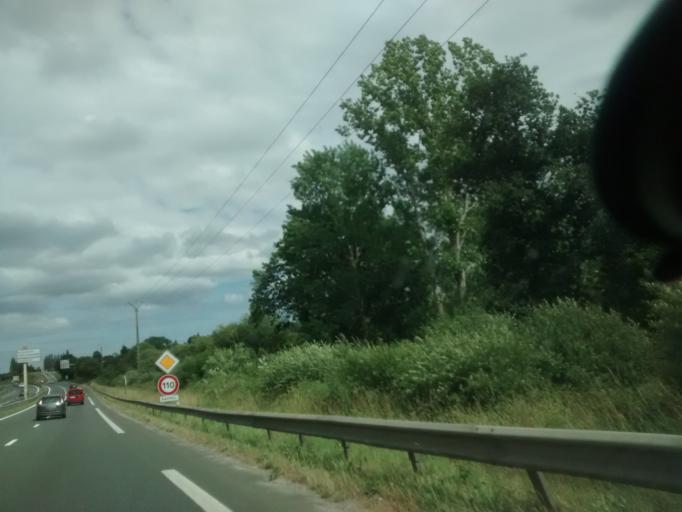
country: FR
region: Brittany
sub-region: Departement des Cotes-d'Armor
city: Guingamp
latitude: 48.5489
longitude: -3.1549
